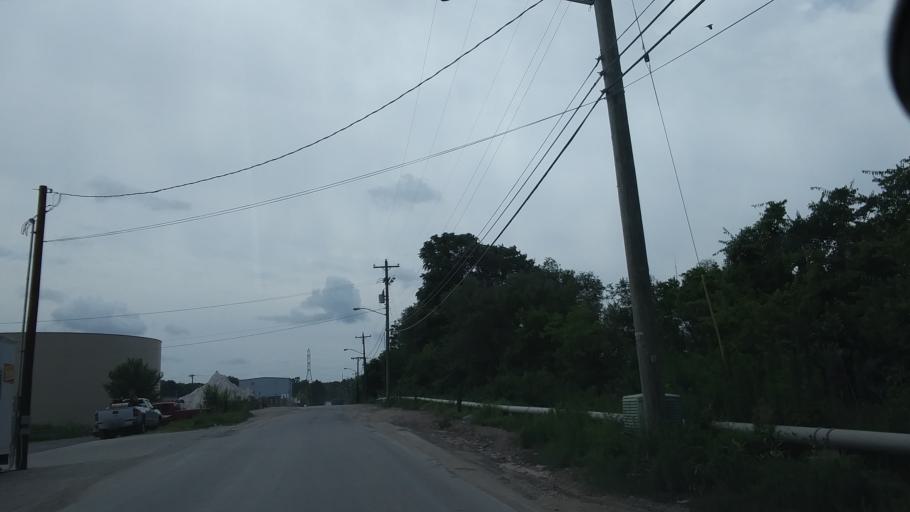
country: US
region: Tennessee
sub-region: Davidson County
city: Belle Meade
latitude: 36.1612
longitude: -86.8841
